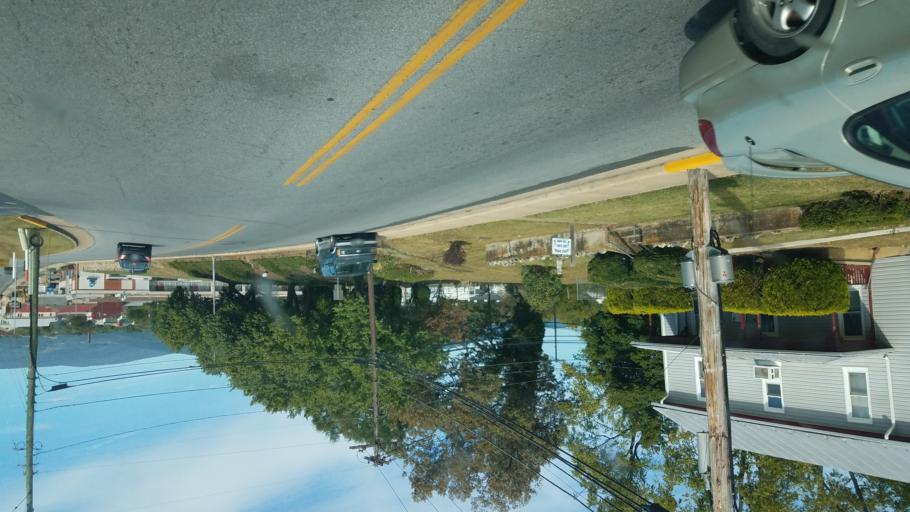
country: US
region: Virginia
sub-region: Page County
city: Luray
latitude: 38.6654
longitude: -78.4690
